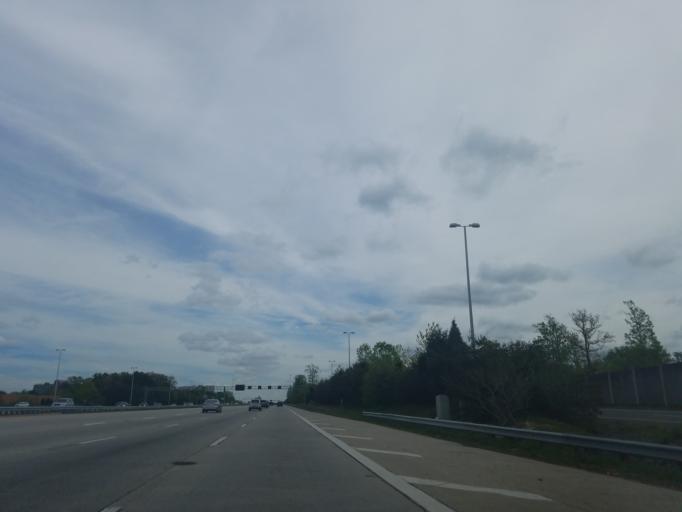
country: US
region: Virginia
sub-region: Fairfax County
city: Greenbriar
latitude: 38.8529
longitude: -77.3959
